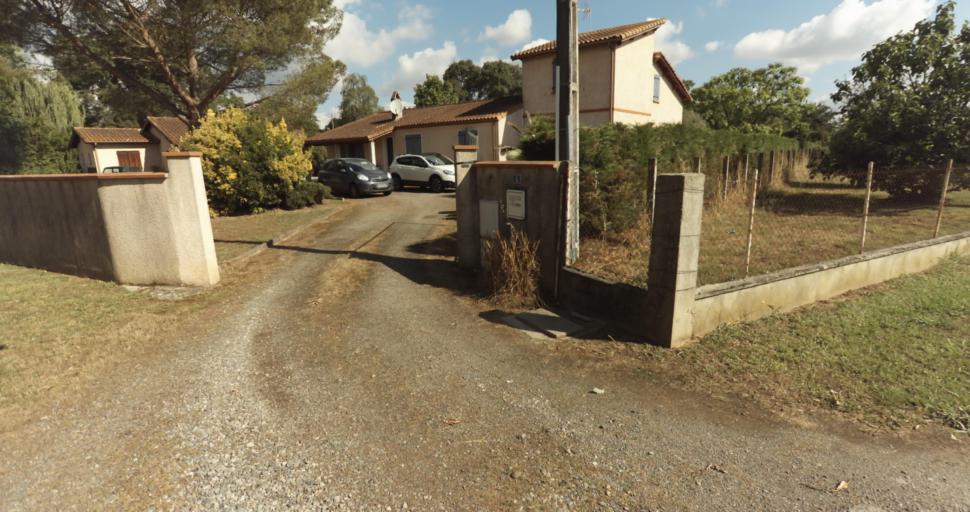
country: FR
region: Midi-Pyrenees
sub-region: Departement de la Haute-Garonne
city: Fonsorbes
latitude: 43.5606
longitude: 1.2289
